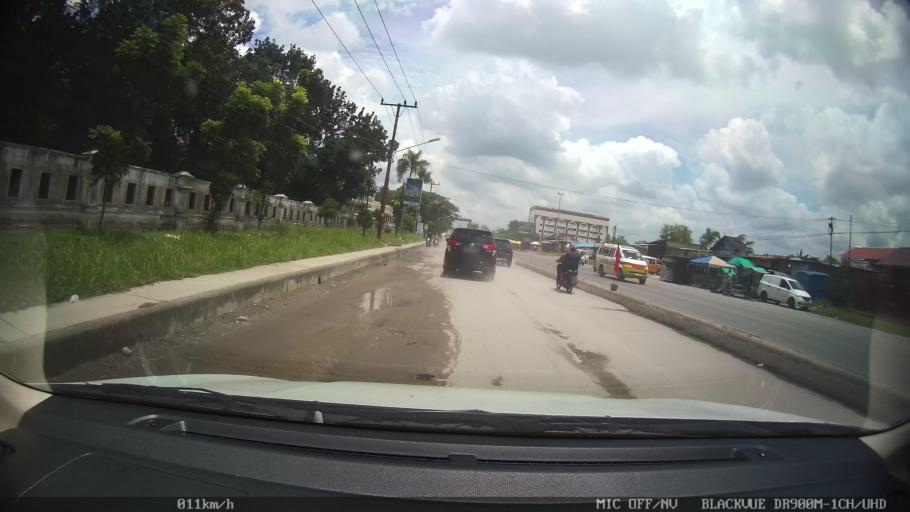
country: ID
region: North Sumatra
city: Medan
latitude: 3.6061
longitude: 98.7185
